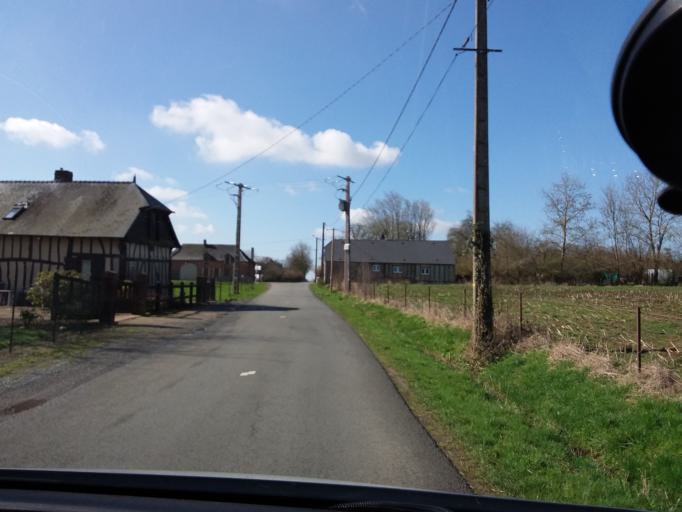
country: FR
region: Picardie
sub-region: Departement de l'Aisne
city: Origny-en-Thierache
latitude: 49.8385
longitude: 4.0625
